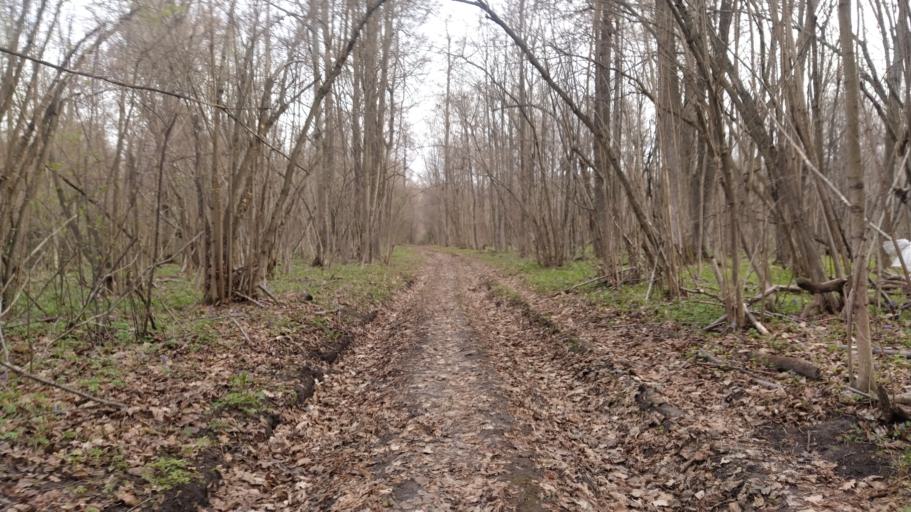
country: RU
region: Chuvashia
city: Novyye Lapsary
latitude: 56.1335
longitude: 47.1215
